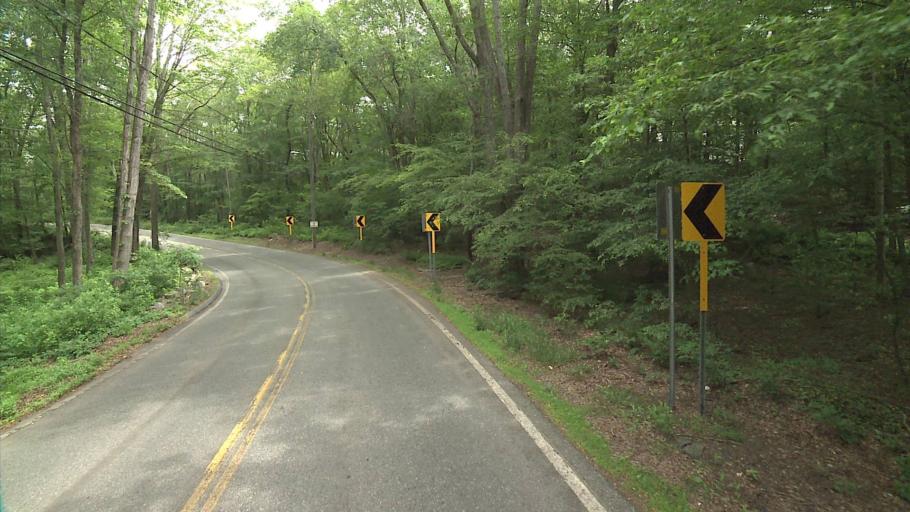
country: US
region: Connecticut
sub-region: New London County
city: Ledyard Center
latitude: 41.4555
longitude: -71.9626
